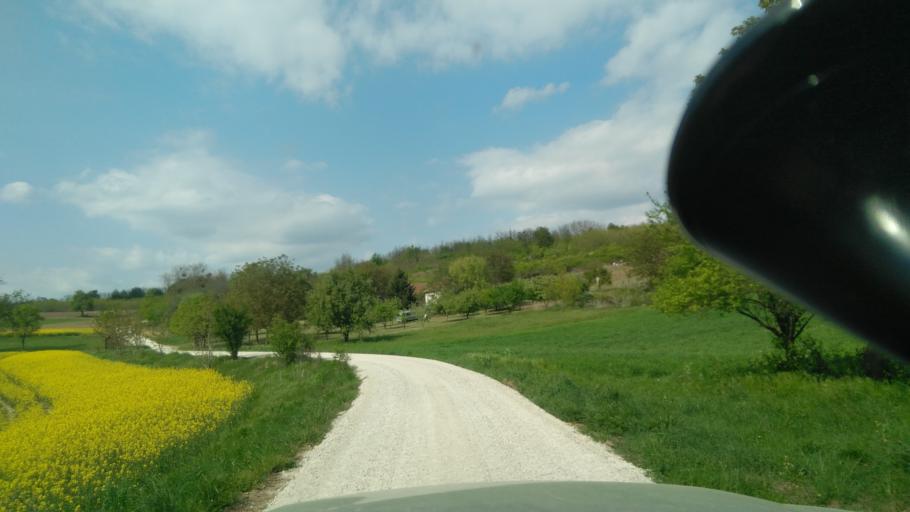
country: HU
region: Zala
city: Pacsa
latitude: 46.7715
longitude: 17.0762
